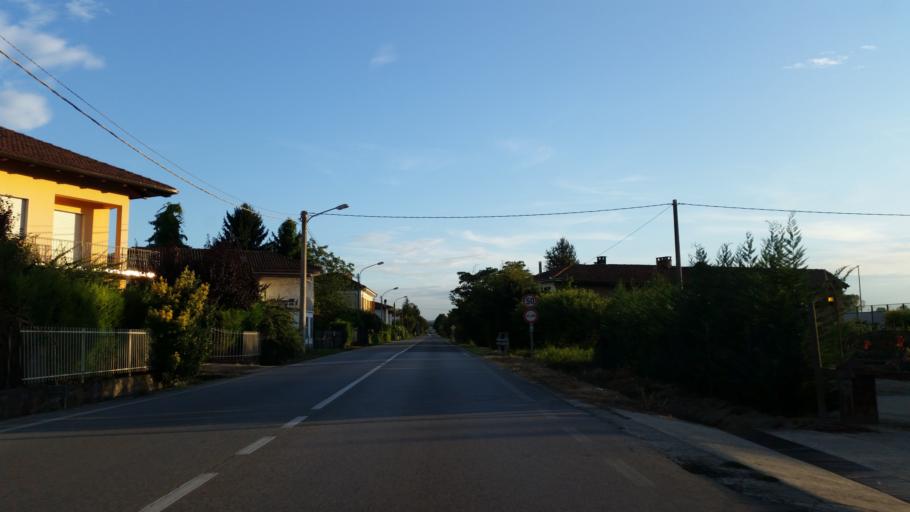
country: IT
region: Piedmont
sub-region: Provincia di Asti
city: Mongardino
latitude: 44.8601
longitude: 8.2038
